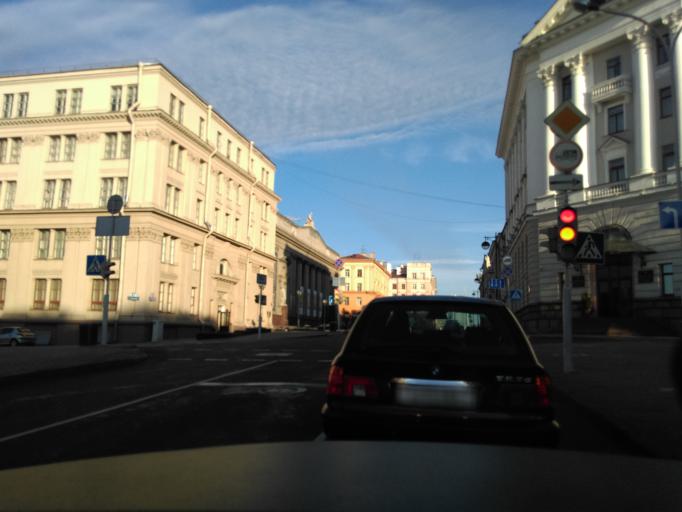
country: BY
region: Minsk
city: Minsk
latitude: 53.8980
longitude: 27.5623
